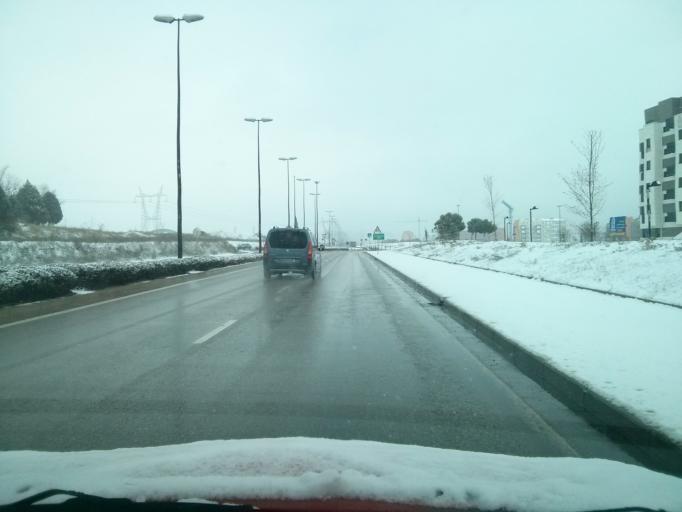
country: ES
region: Castille and Leon
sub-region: Provincia de Burgos
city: Burgos
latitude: 42.3658
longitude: -3.6740
